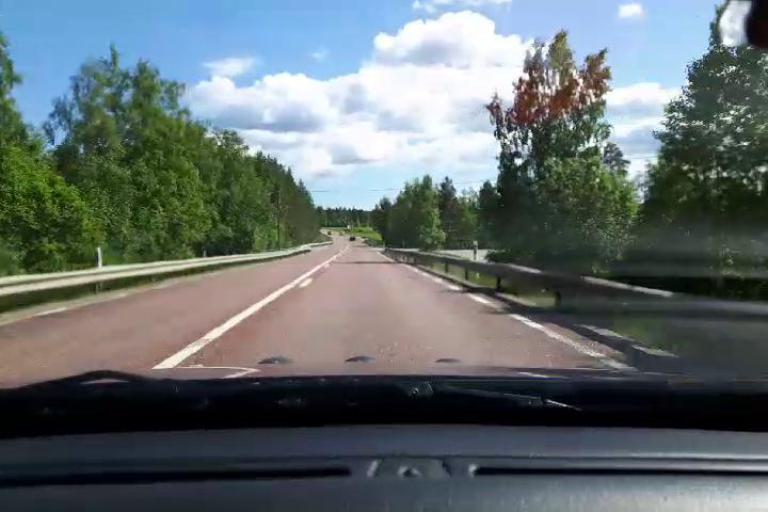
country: SE
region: Gaevleborg
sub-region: Hudiksvalls Kommun
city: Delsbo
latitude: 61.7843
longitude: 16.6344
